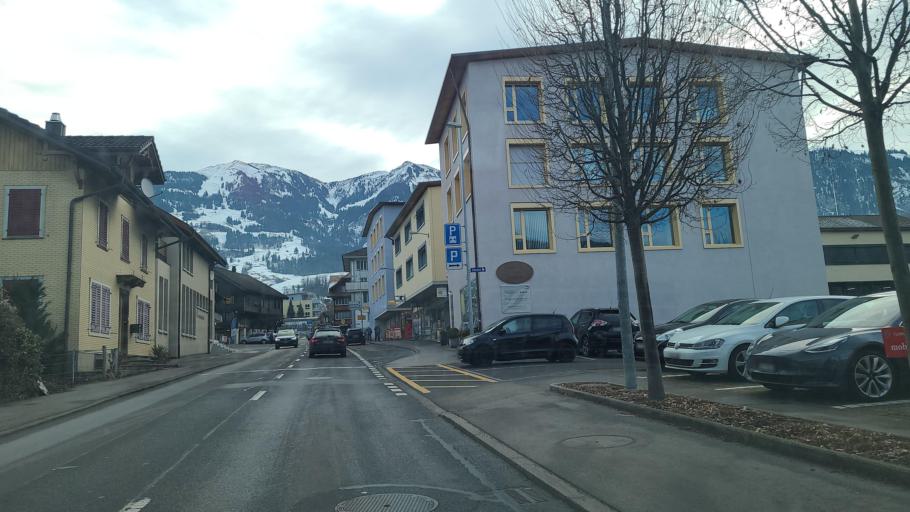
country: CH
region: Obwalden
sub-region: Obwalden
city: Kerns
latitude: 46.9012
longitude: 8.2737
